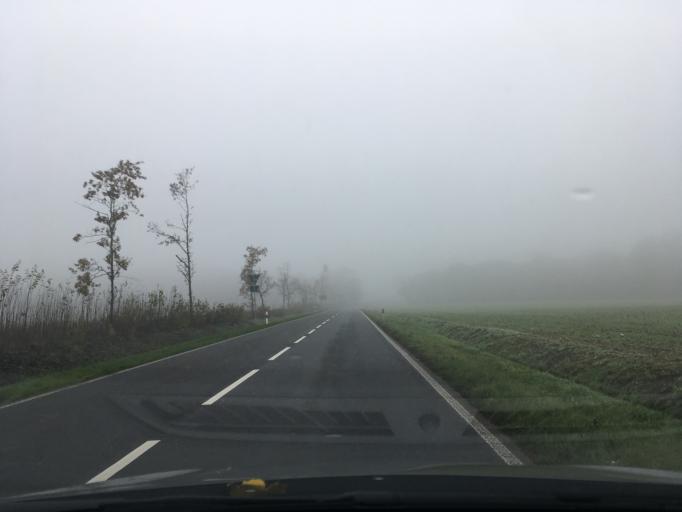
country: DE
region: North Rhine-Westphalia
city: Stadtlohn
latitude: 52.0542
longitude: 6.9469
